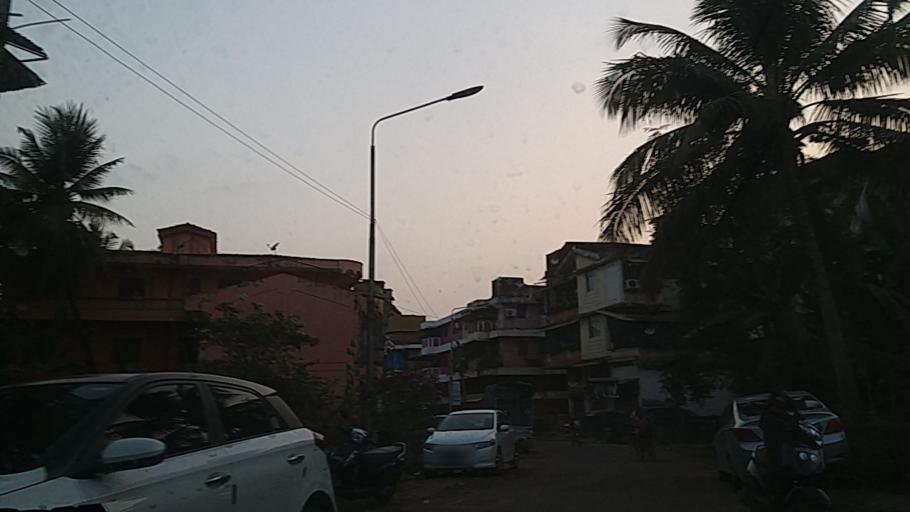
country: IN
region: Goa
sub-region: South Goa
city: Madgaon
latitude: 15.2617
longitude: 73.9646
